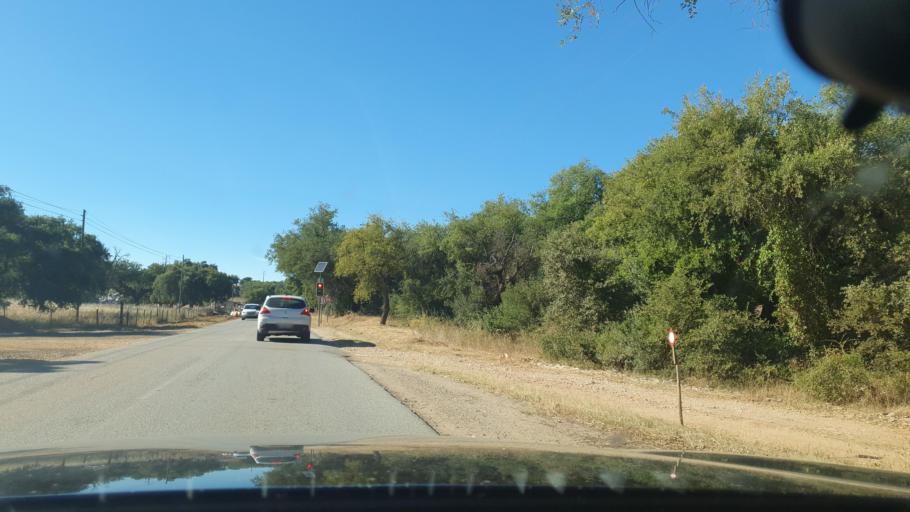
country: PT
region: Evora
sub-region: Alandroal
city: Alandroal
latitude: 38.7396
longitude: -7.4044
